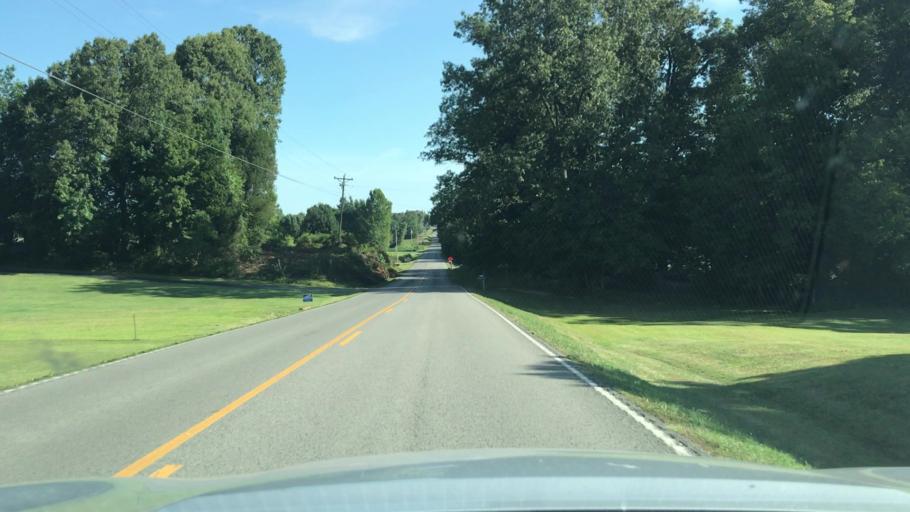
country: US
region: Kentucky
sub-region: Muhlenberg County
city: Greenville
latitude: 37.1484
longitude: -87.1413
